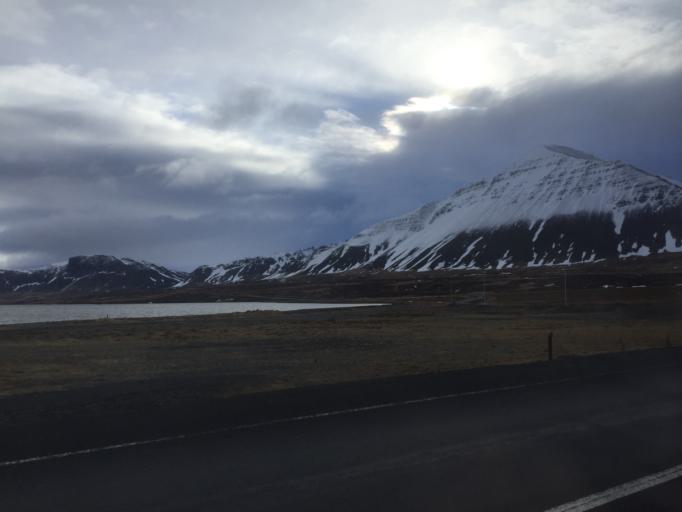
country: IS
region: West
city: Borgarnes
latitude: 64.5281
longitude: -21.8840
